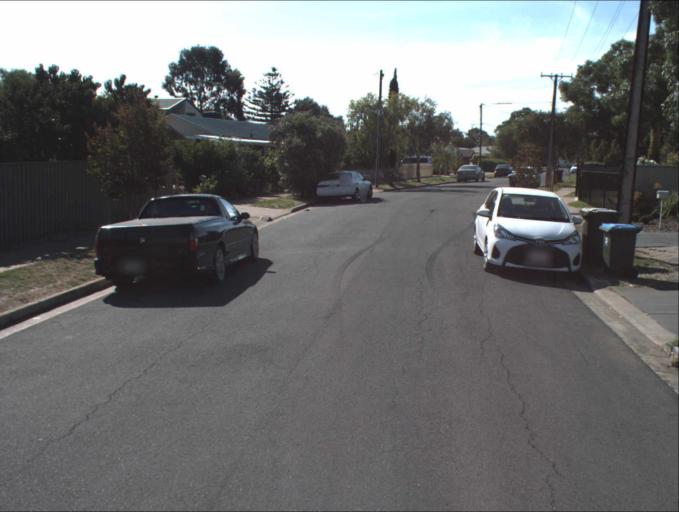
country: AU
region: South Australia
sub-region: Port Adelaide Enfield
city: Gilles Plains
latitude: -34.8644
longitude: 138.6429
